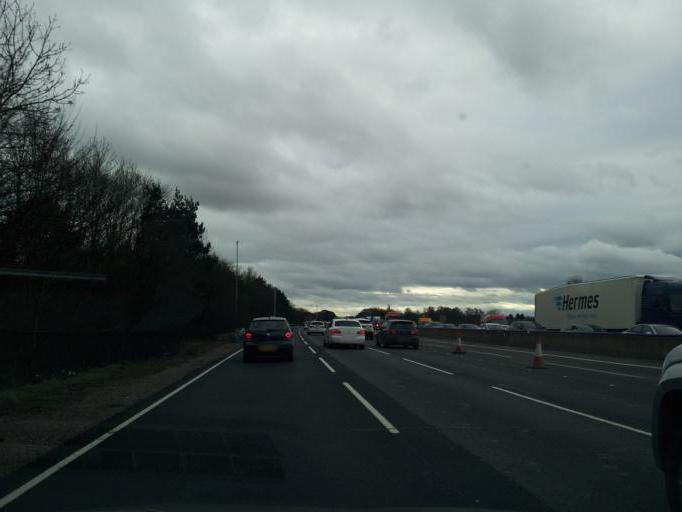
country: GB
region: England
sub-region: Staffordshire
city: Penkridge
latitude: 52.7318
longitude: -2.0981
